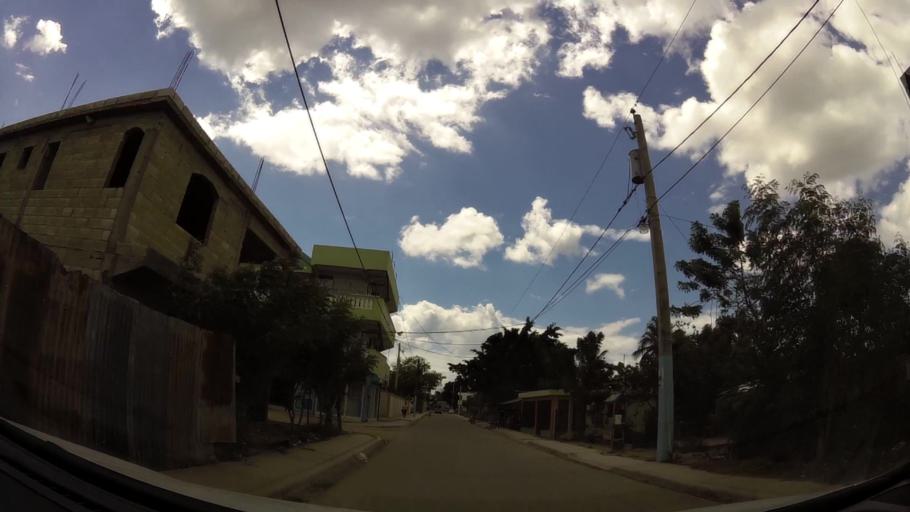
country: DO
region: Santo Domingo
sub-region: Santo Domingo
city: Boca Chica
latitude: 18.4511
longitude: -69.6522
